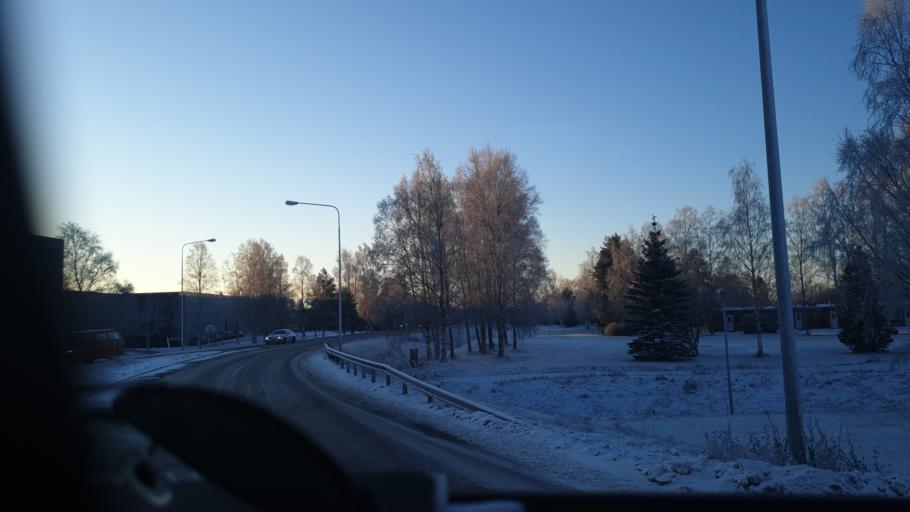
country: FI
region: Northern Ostrobothnia
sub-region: Ylivieska
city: Kalajoki
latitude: 64.2610
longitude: 23.9467
